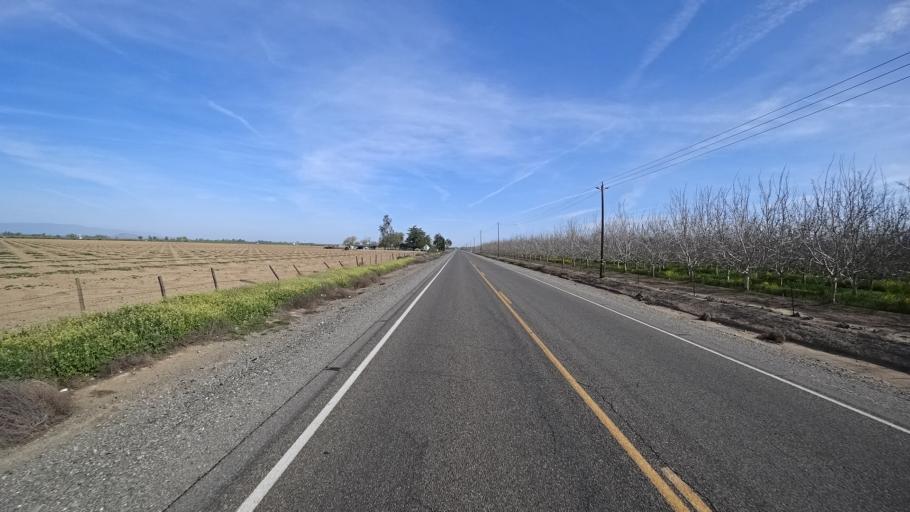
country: US
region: California
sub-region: Glenn County
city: Orland
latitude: 39.6542
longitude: -122.1972
